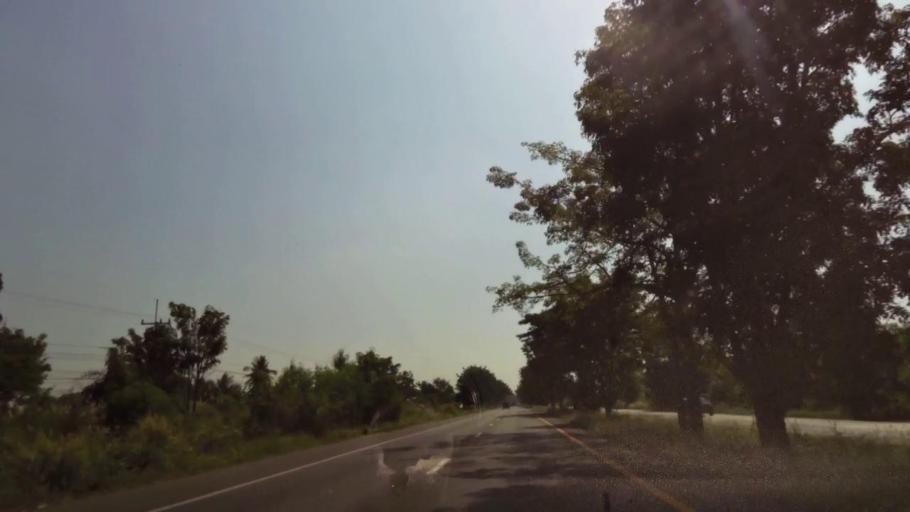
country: TH
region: Nakhon Sawan
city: Kao Liao
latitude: 15.9735
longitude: 100.1191
